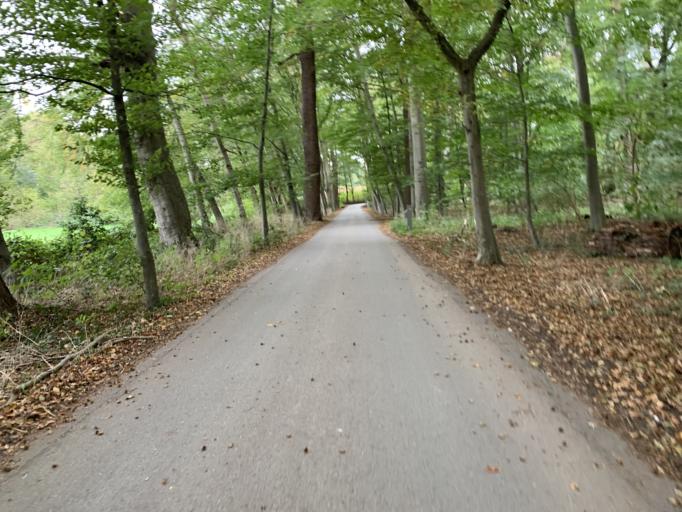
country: DE
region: North Rhine-Westphalia
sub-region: Regierungsbezirk Munster
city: Rheine
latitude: 52.3015
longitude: 7.4255
